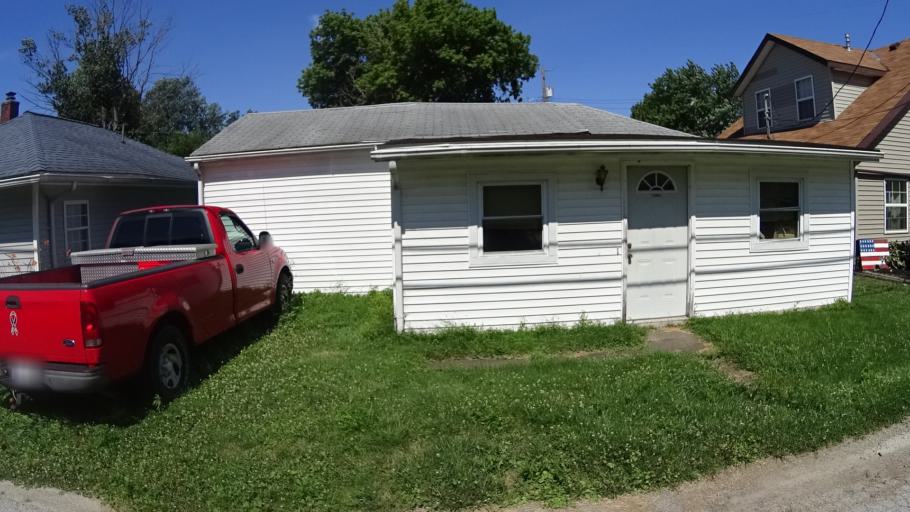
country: US
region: Ohio
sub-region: Ottawa County
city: Port Clinton
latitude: 41.4313
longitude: -82.8990
